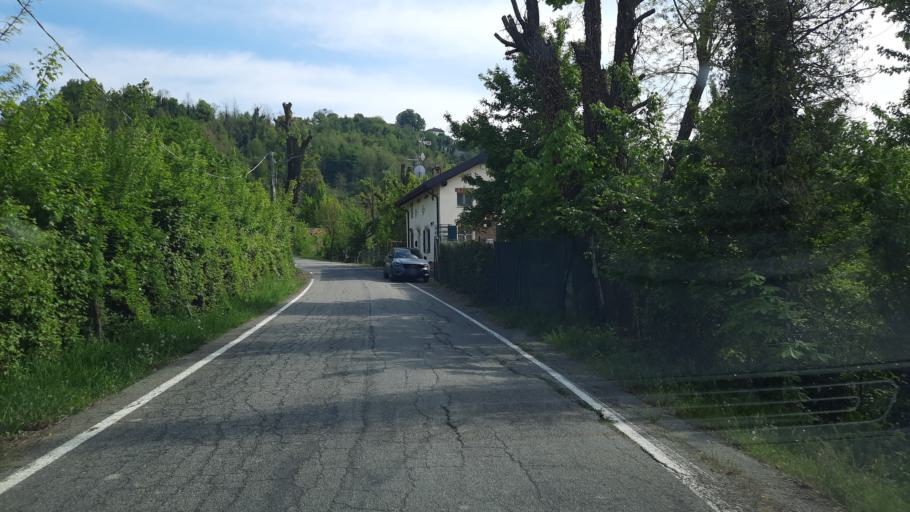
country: IT
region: Piedmont
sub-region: Provincia di Alessandria
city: Camino
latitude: 45.1669
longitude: 8.2622
